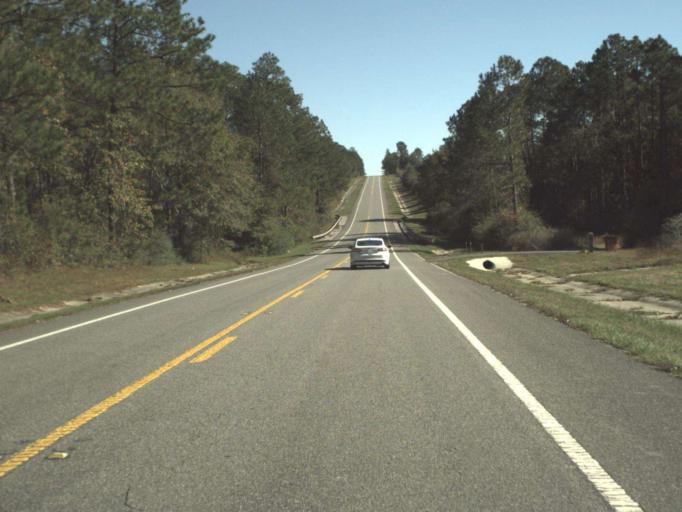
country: US
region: Florida
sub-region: Okaloosa County
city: Crestview
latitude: 30.8504
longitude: -86.7832
